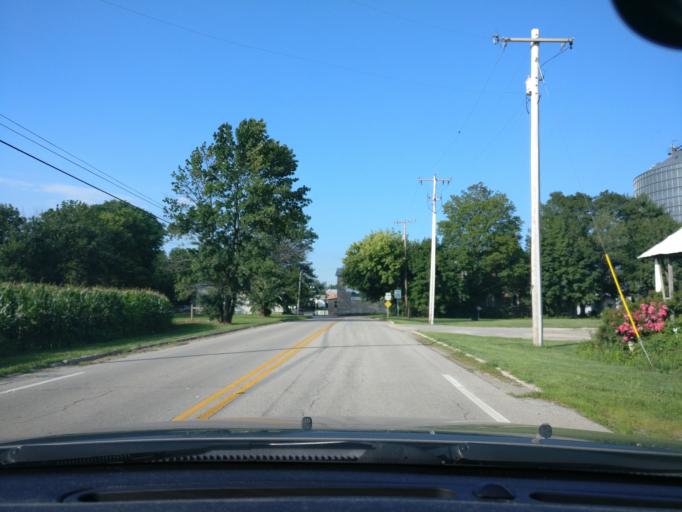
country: US
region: Ohio
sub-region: Greene County
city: Shawnee Hills
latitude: 39.5502
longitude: -83.7890
